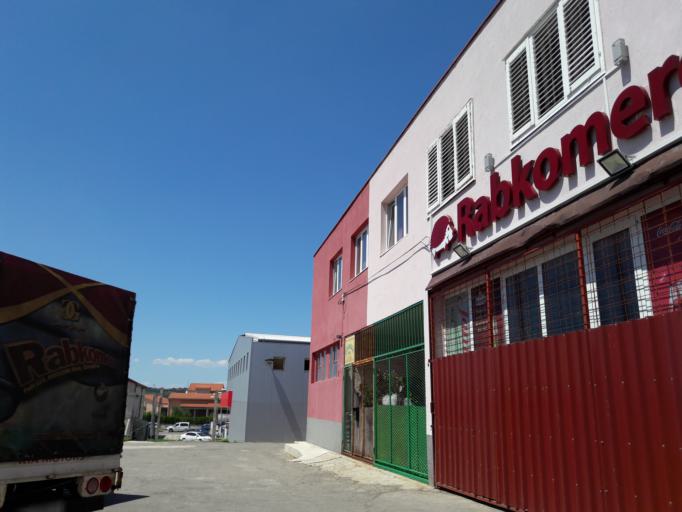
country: HR
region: Primorsko-Goranska
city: Banjol
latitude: 44.7632
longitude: 14.7596
